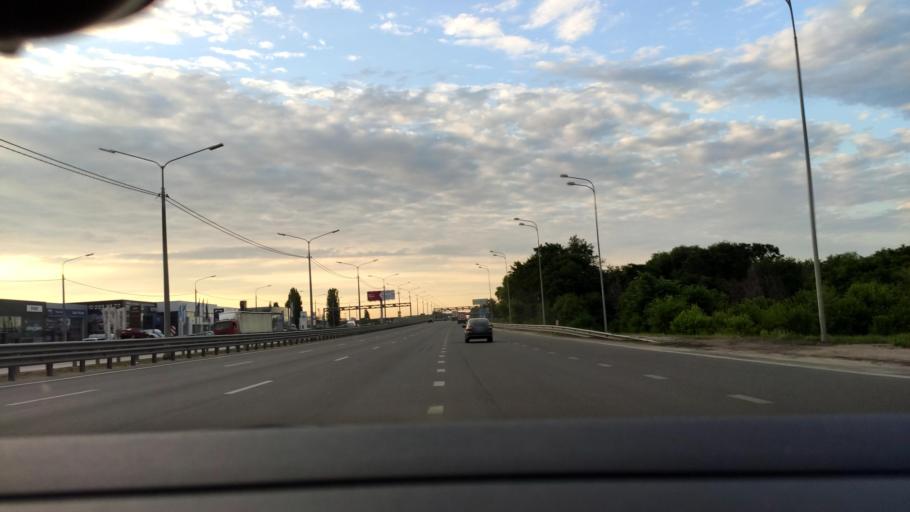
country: RU
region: Voronezj
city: Podgornoye
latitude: 51.7932
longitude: 39.2012
